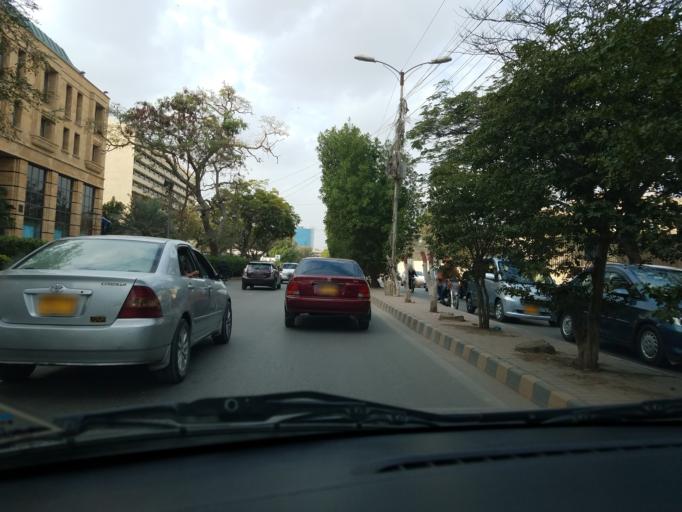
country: PK
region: Sindh
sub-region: Karachi District
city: Karachi
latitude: 24.8448
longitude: 67.0320
